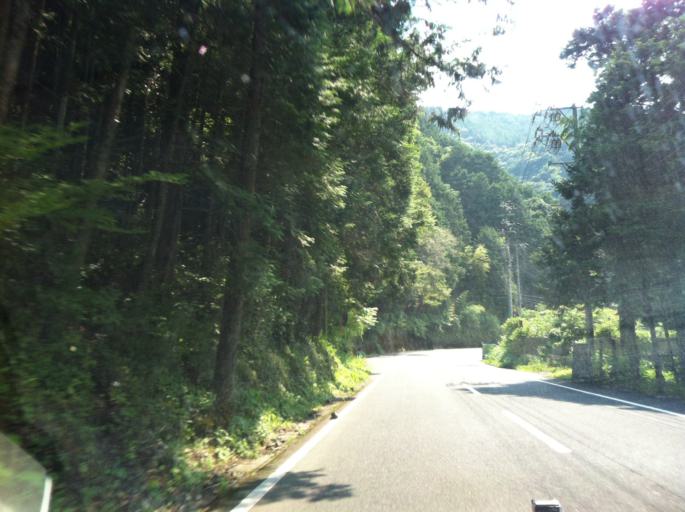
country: JP
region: Shizuoka
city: Shizuoka-shi
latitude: 35.1290
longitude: 138.3693
